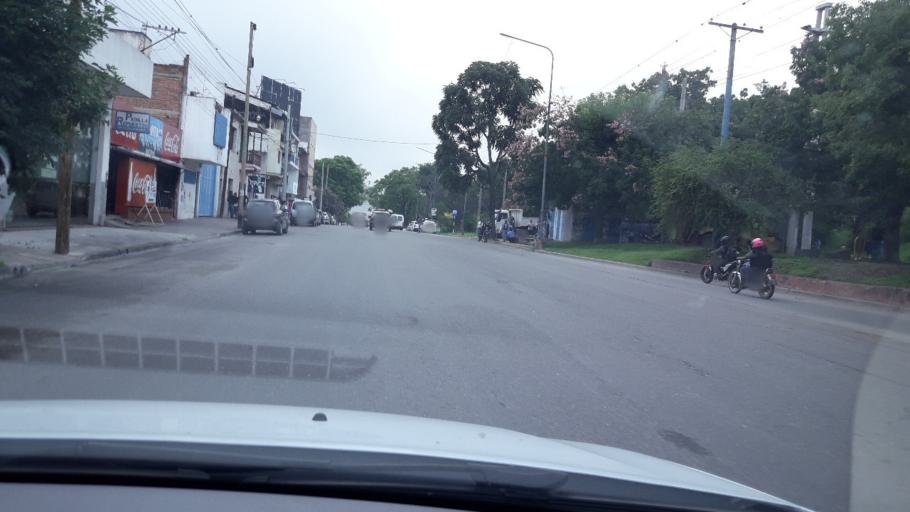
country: AR
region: Jujuy
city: San Salvador de Jujuy
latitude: -24.1972
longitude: -65.2899
